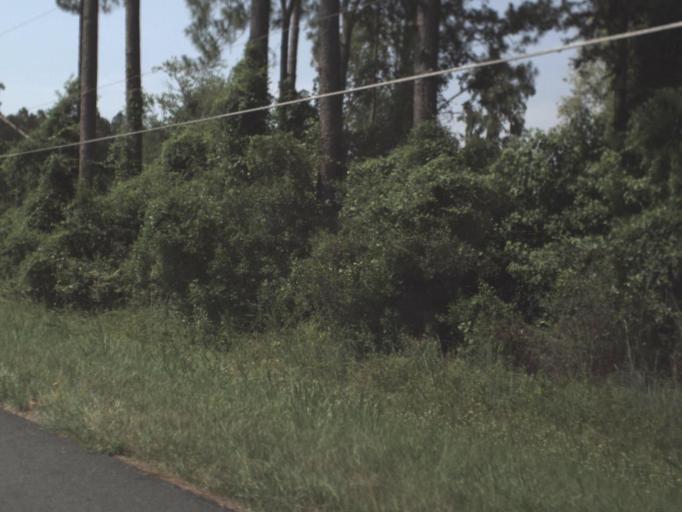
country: US
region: Florida
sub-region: Hamilton County
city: Jasper
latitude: 30.5320
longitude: -82.9699
